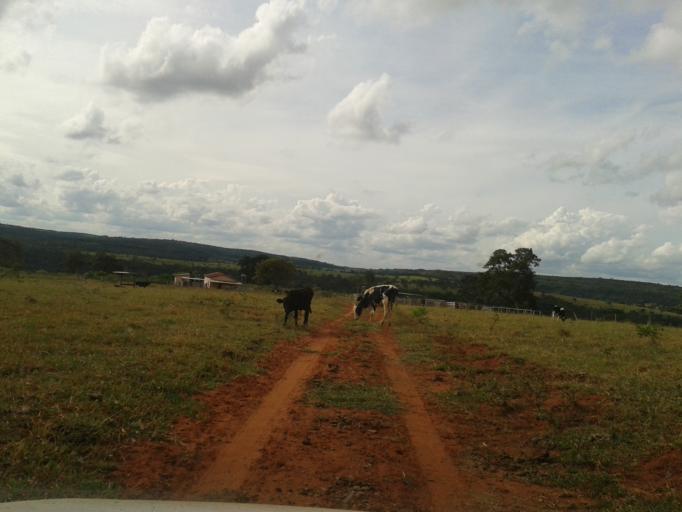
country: BR
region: Minas Gerais
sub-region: Campina Verde
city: Campina Verde
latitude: -19.4467
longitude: -49.6128
